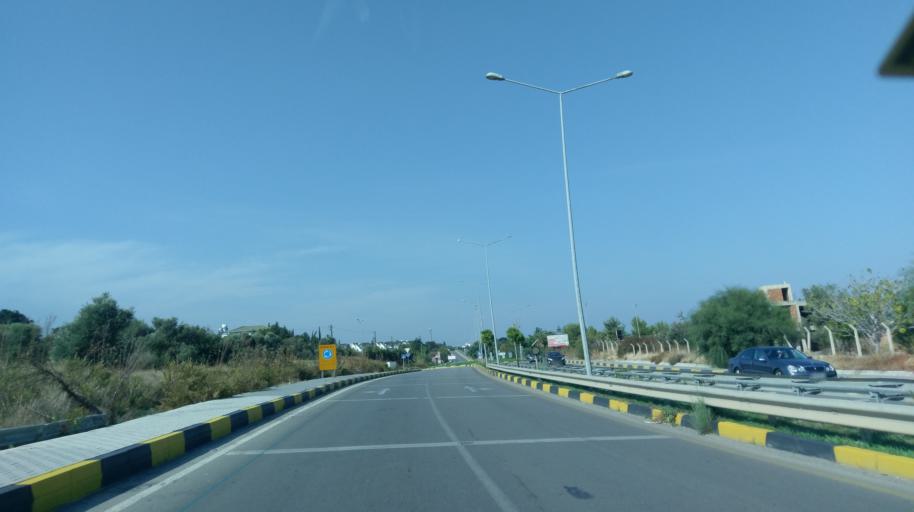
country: CY
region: Keryneia
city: Kyrenia
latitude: 35.3344
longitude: 33.2639
